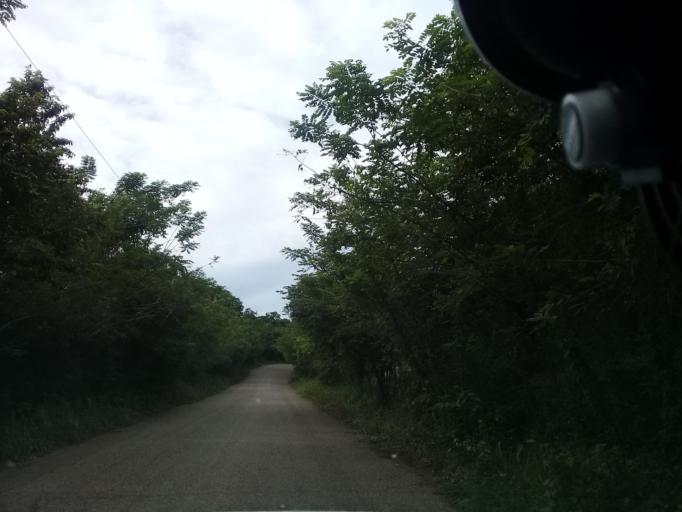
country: MX
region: Veracruz
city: Platon Sanchez
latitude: 21.2142
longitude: -98.3667
